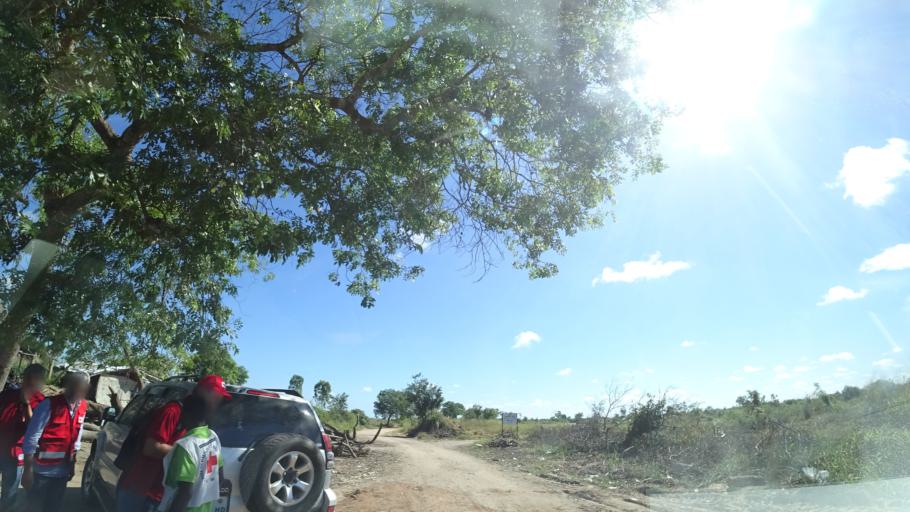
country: MZ
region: Sofala
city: Dondo
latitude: -19.2721
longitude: 34.6793
